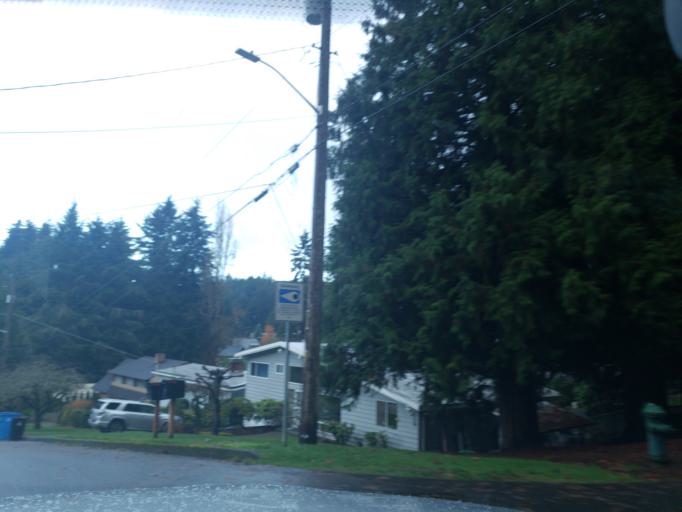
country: US
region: Washington
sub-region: King County
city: Shoreline
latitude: 47.7541
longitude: -122.3563
